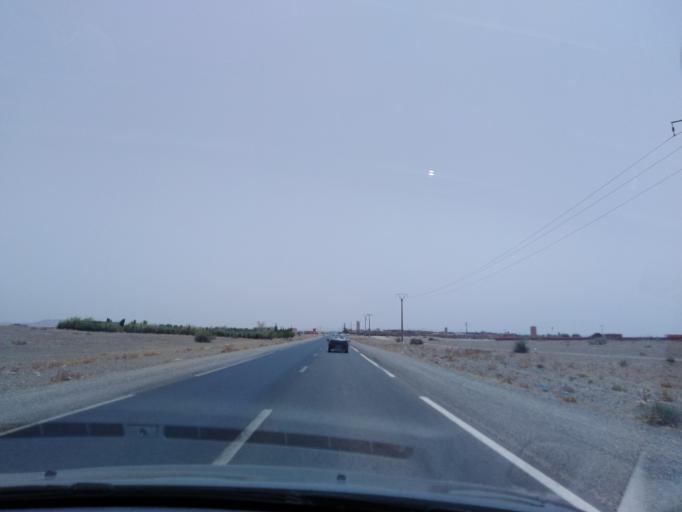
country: MA
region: Marrakech-Tensift-Al Haouz
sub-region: Marrakech
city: Marrakesh
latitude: 31.8064
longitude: -8.1514
